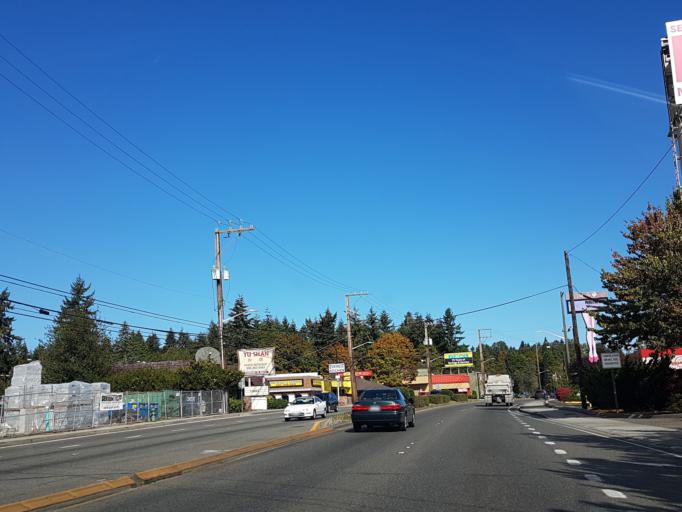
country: US
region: Washington
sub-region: King County
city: Lake Forest Park
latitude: 47.7346
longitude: -122.2924
